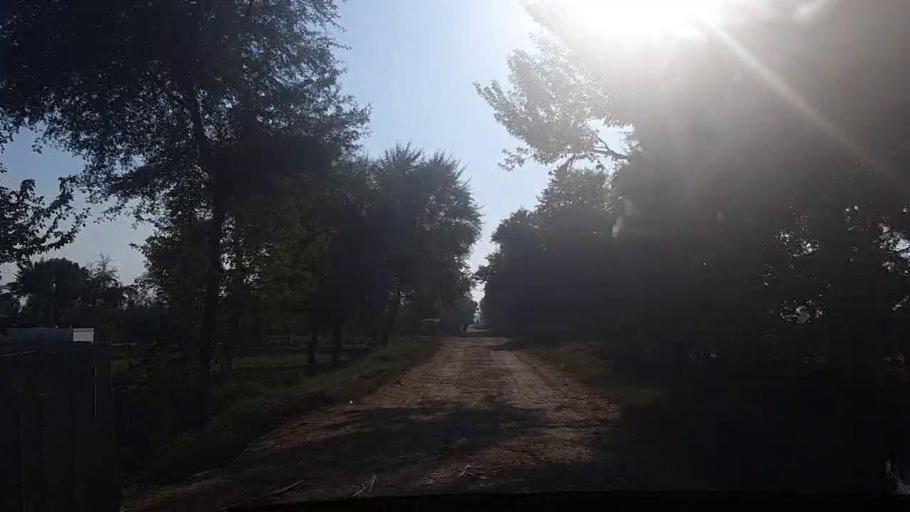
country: PK
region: Sindh
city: Gambat
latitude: 27.3761
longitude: 68.4668
